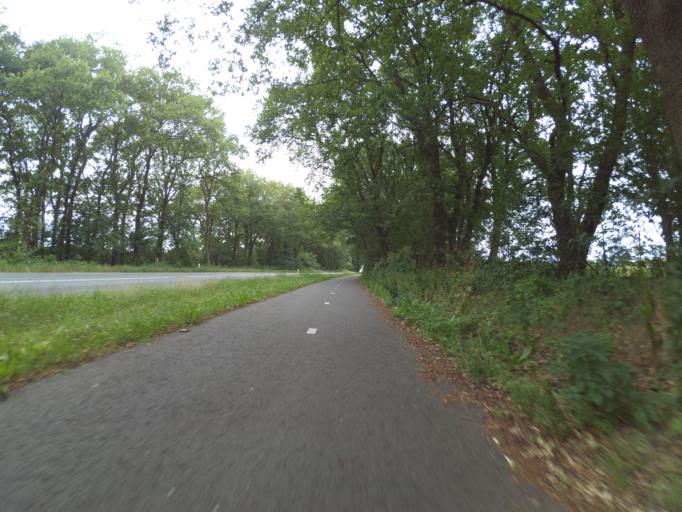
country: NL
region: Gelderland
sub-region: Gemeente Renkum
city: Wolfheze
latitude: 52.0458
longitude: 5.8077
